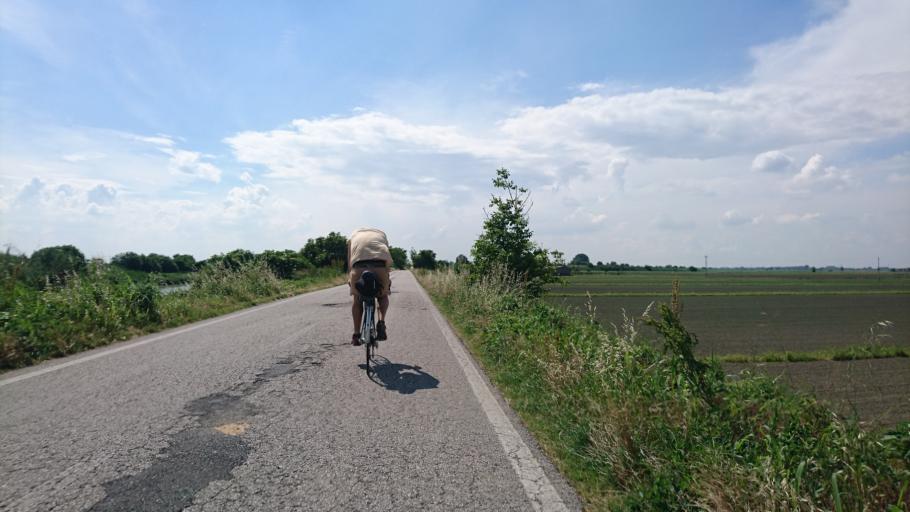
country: IT
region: Veneto
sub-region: Provincia di Rovigo
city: Ceneselli
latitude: 45.0727
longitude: 11.3483
